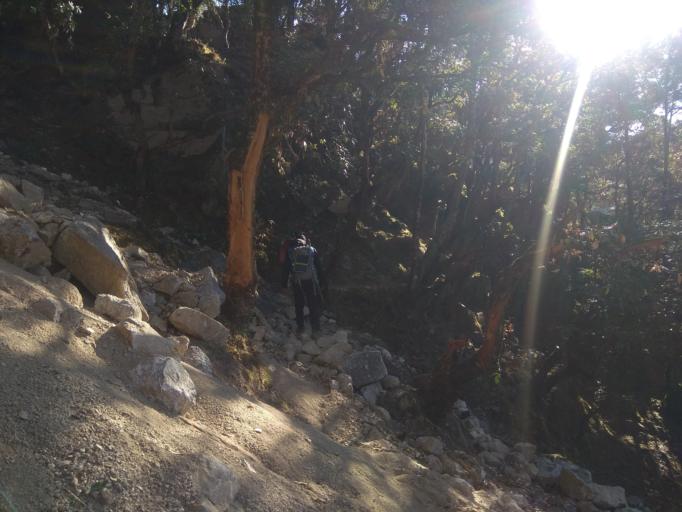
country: NP
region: Far Western
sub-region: Seti Zone
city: Achham
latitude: 29.2743
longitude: 81.6132
